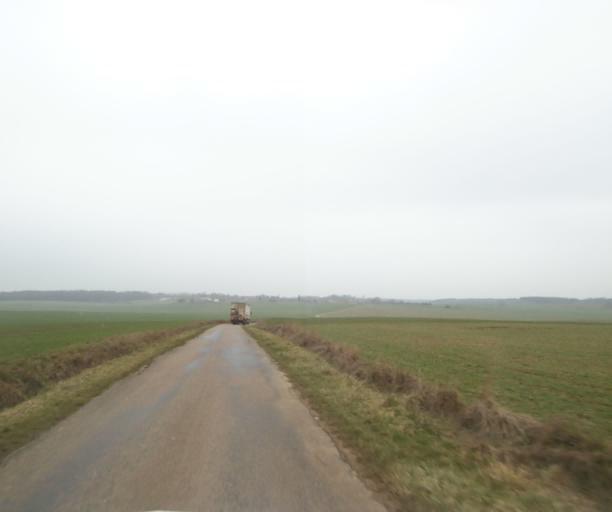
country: FR
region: Champagne-Ardenne
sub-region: Departement de la Haute-Marne
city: Chevillon
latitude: 48.5011
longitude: 5.0799
